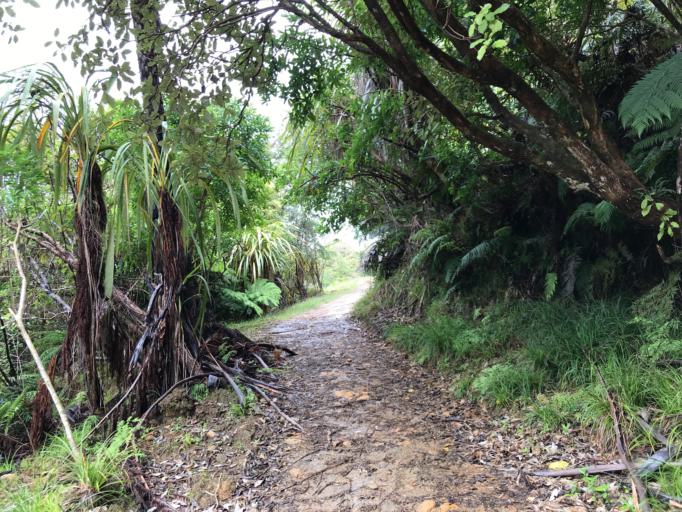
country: NZ
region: Marlborough
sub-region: Marlborough District
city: Picton
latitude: -41.1152
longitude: 174.1634
